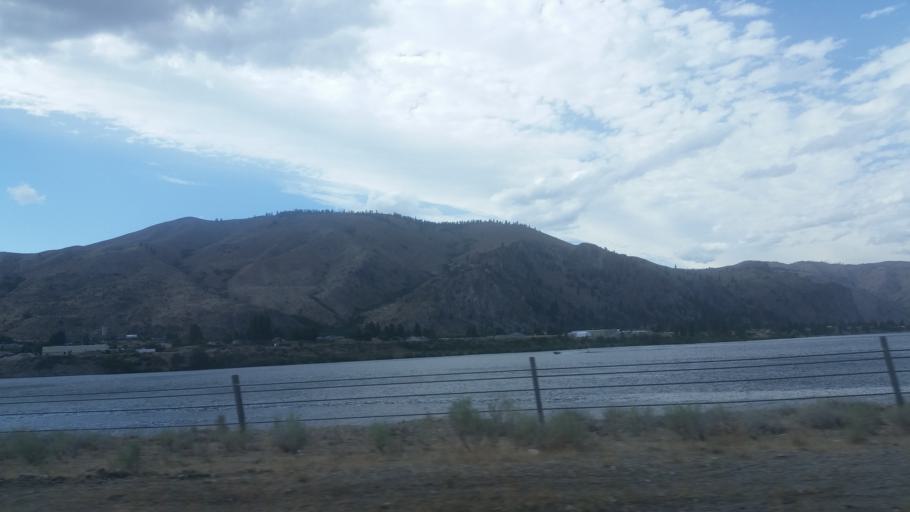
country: US
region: Washington
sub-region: Chelan County
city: Entiat
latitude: 47.6818
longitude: -120.1944
